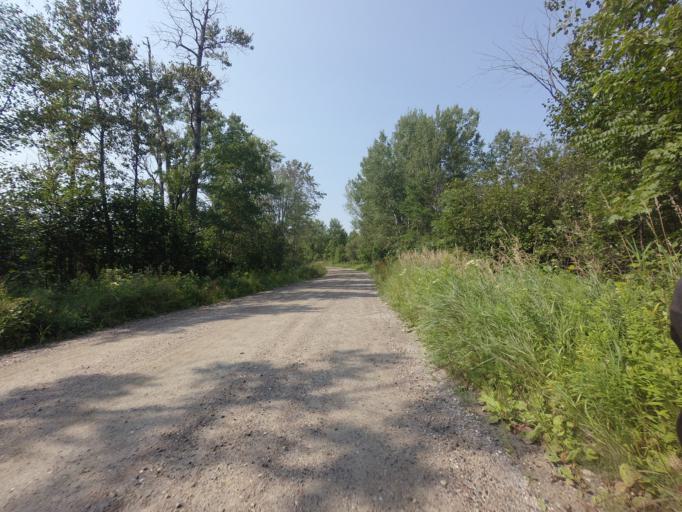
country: CA
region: Ontario
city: Skatepark
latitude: 44.7136
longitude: -76.7680
